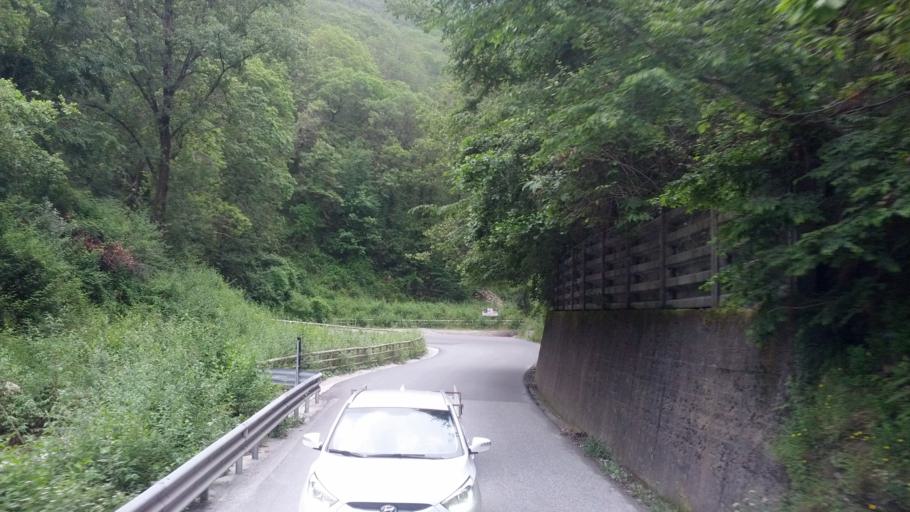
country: IT
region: Tuscany
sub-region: Provincia di Massa-Carrara
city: Massa
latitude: 44.0772
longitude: 10.1312
